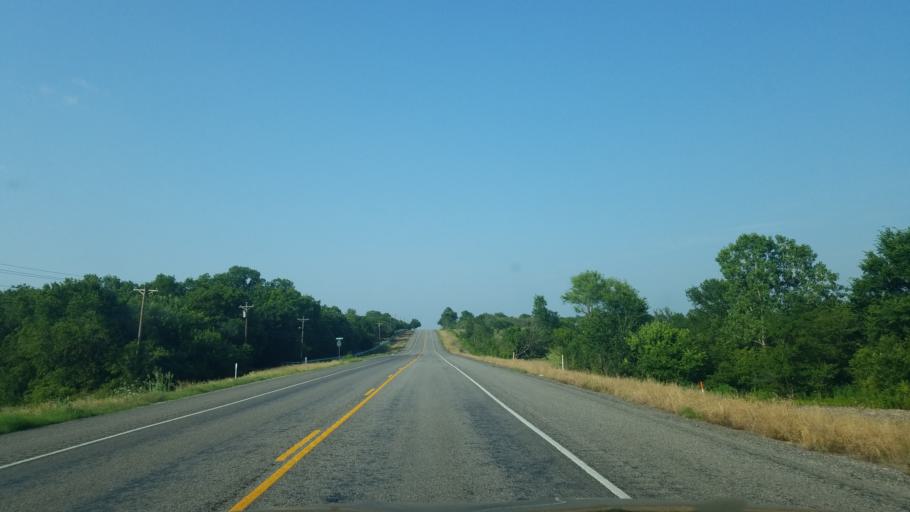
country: US
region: Texas
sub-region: Denton County
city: Denton
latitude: 33.2886
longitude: -97.0839
